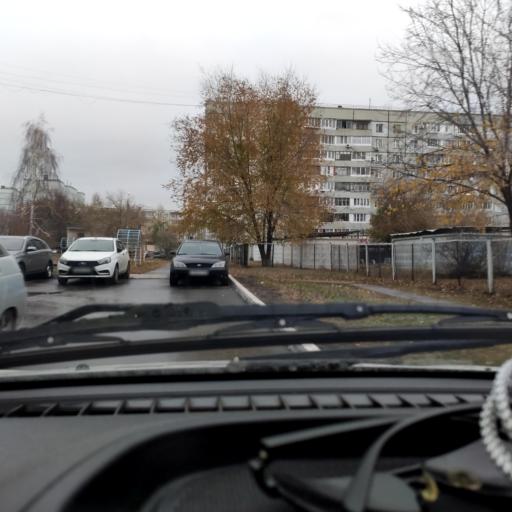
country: RU
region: Samara
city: Zhigulevsk
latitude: 53.4735
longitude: 49.5142
